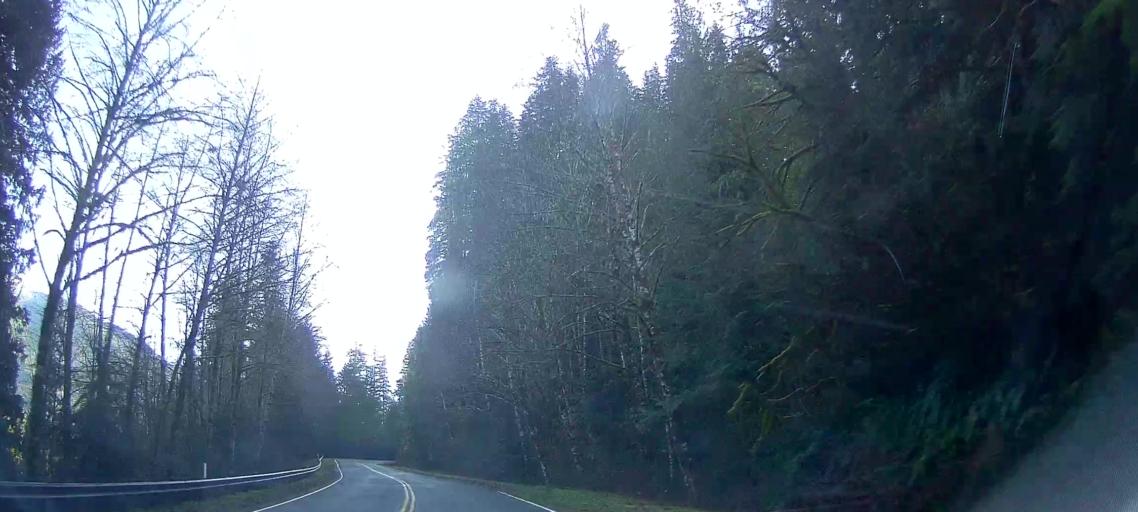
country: US
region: Washington
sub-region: Snohomish County
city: Darrington
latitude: 48.6544
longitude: -121.7111
